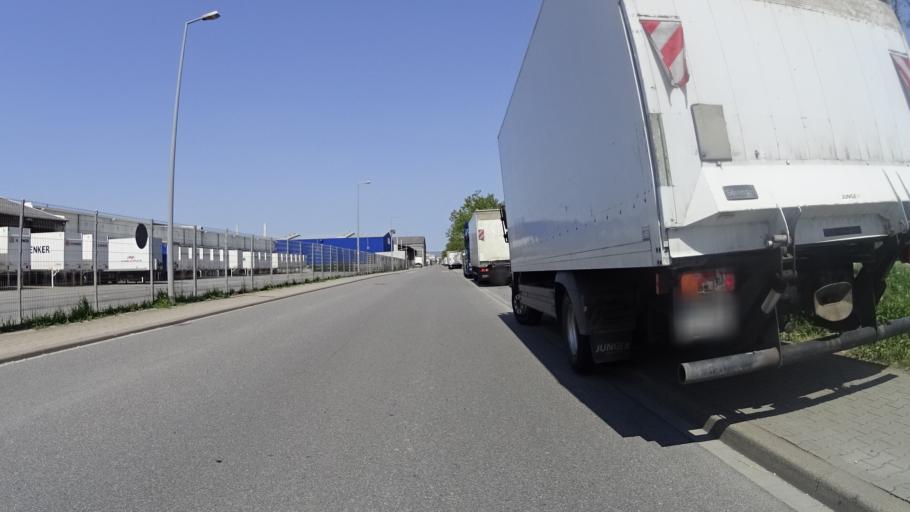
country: DE
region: Rheinland-Pfalz
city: Altrip
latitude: 49.4238
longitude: 8.5191
